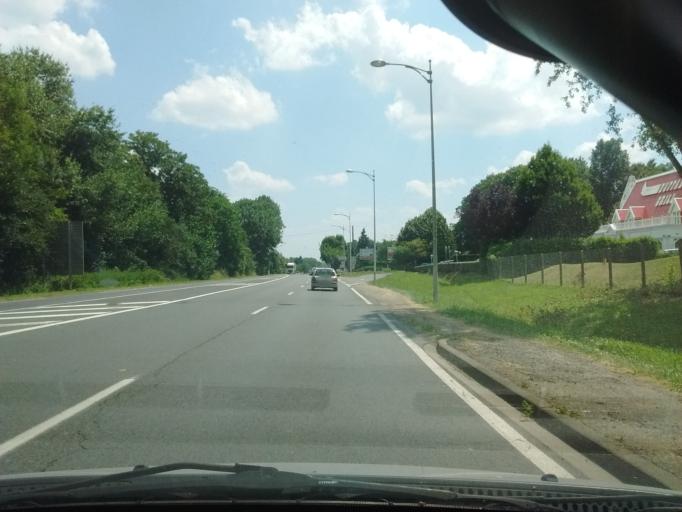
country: FR
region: Ile-de-France
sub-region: Departement de Seine-et-Marne
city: Ponthierry
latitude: 48.5355
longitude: 2.5291
